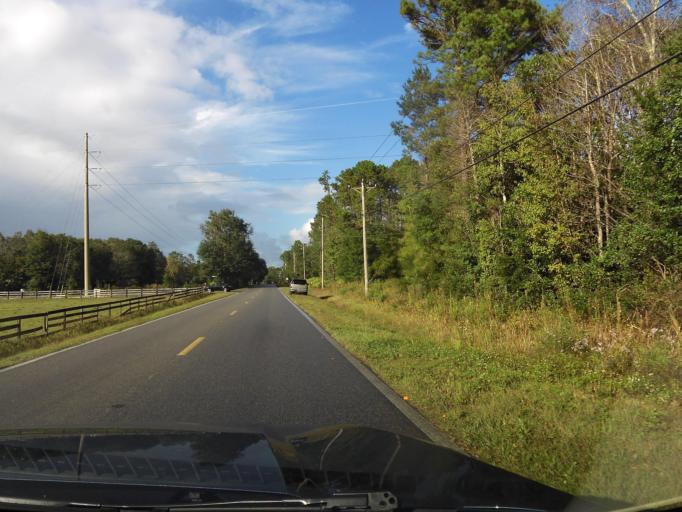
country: US
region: Florida
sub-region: Clay County
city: Asbury Lake
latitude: 30.0405
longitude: -81.8468
